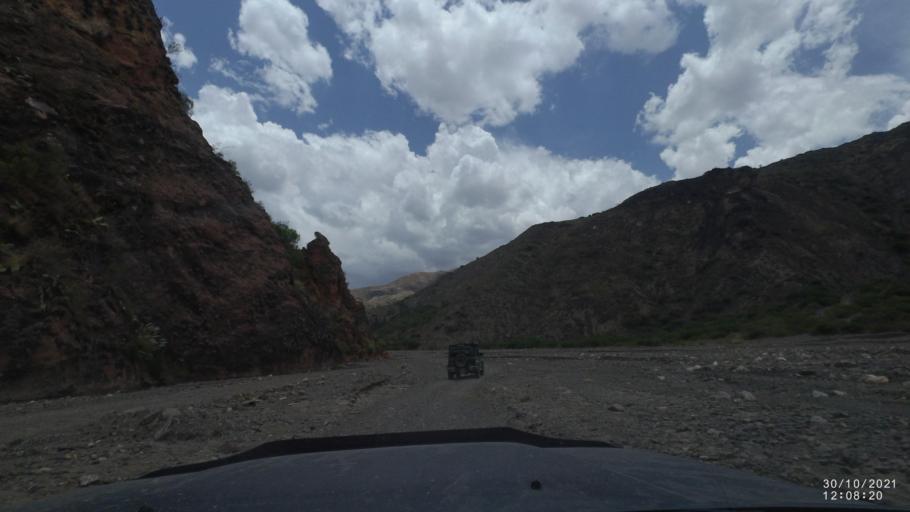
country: BO
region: Cochabamba
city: Colchani
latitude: -17.5419
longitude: -66.6271
